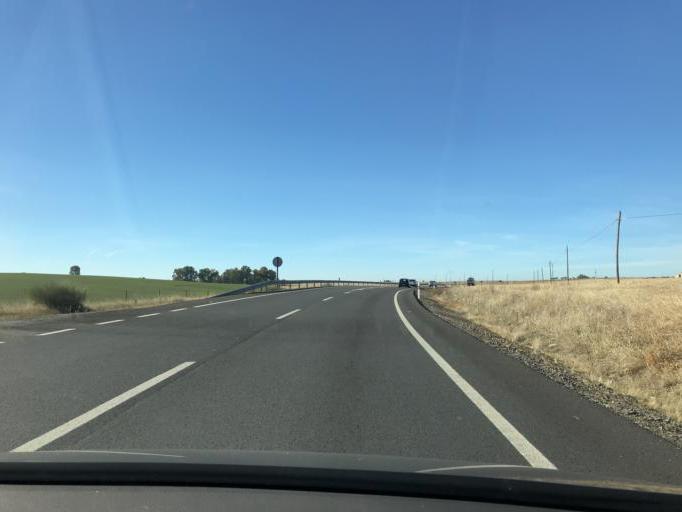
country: ES
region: Extremadura
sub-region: Provincia de Badajoz
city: Granja de Torrehermosa
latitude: 38.3005
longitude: -5.6190
